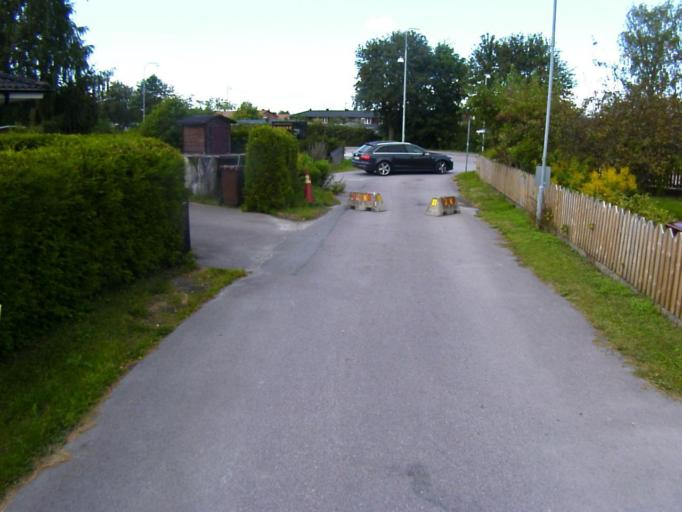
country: SE
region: Soedermanland
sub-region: Eskilstuna Kommun
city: Eskilstuna
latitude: 59.3746
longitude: 16.4768
